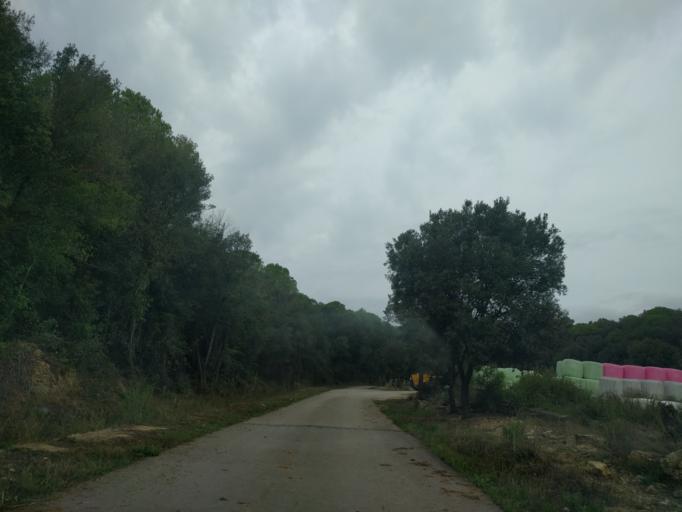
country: ES
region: Catalonia
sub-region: Provincia de Girona
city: la Cellera de Ter
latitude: 42.0183
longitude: 2.6322
